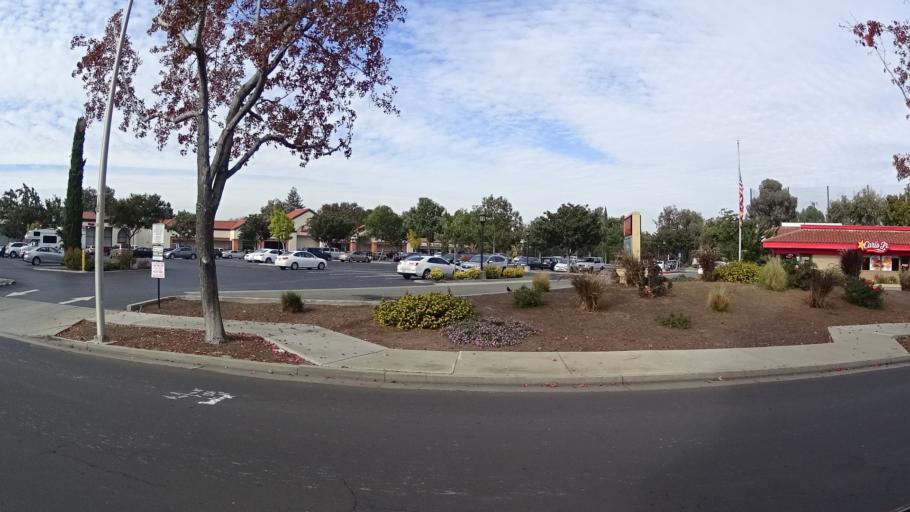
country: US
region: California
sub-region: Santa Clara County
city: Santa Clara
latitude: 37.3290
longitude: -121.9651
